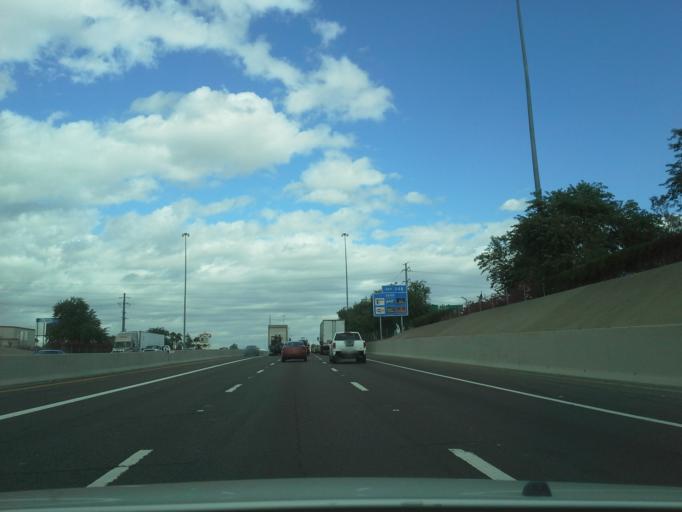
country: US
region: Arizona
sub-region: Maricopa County
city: Glendale
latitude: 33.5689
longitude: -112.1173
